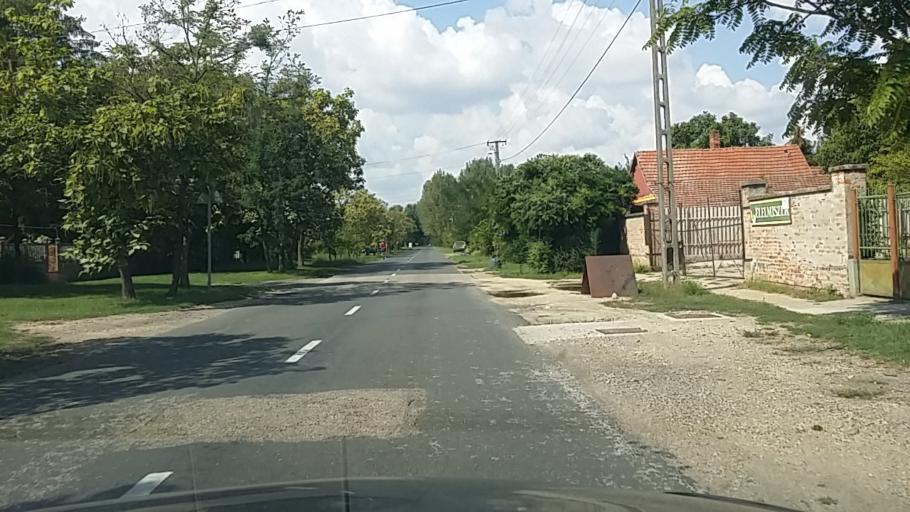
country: HU
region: Bacs-Kiskun
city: Tiszaalpar
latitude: 46.7539
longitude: 20.0331
